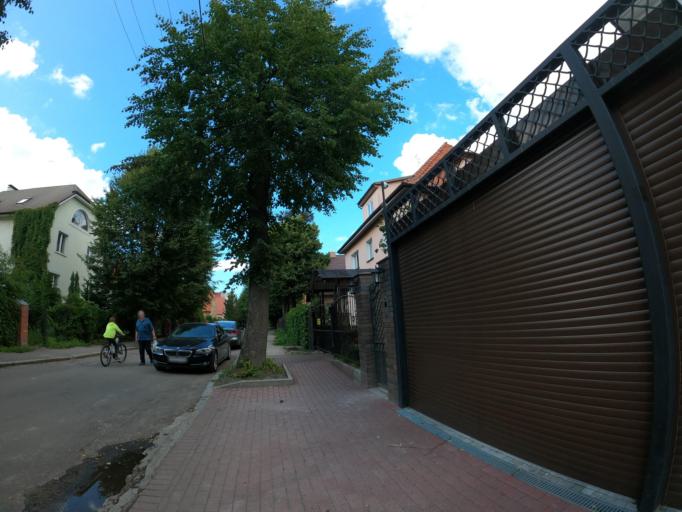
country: RU
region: Kaliningrad
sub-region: Gorod Kaliningrad
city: Kaliningrad
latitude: 54.7309
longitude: 20.4727
